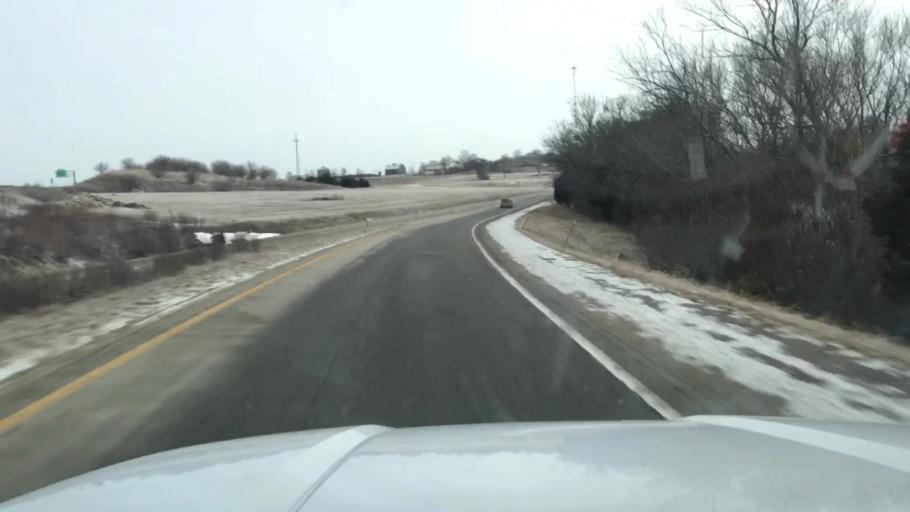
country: US
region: Missouri
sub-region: Andrew County
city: Savannah
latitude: 39.8863
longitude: -94.8557
